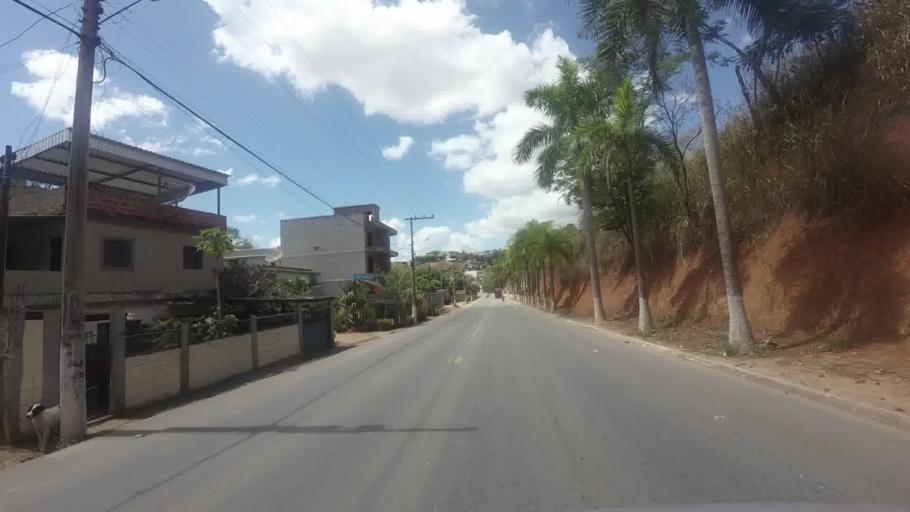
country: BR
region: Minas Gerais
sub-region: Recreio
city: Recreio
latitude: -21.6568
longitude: -42.3541
